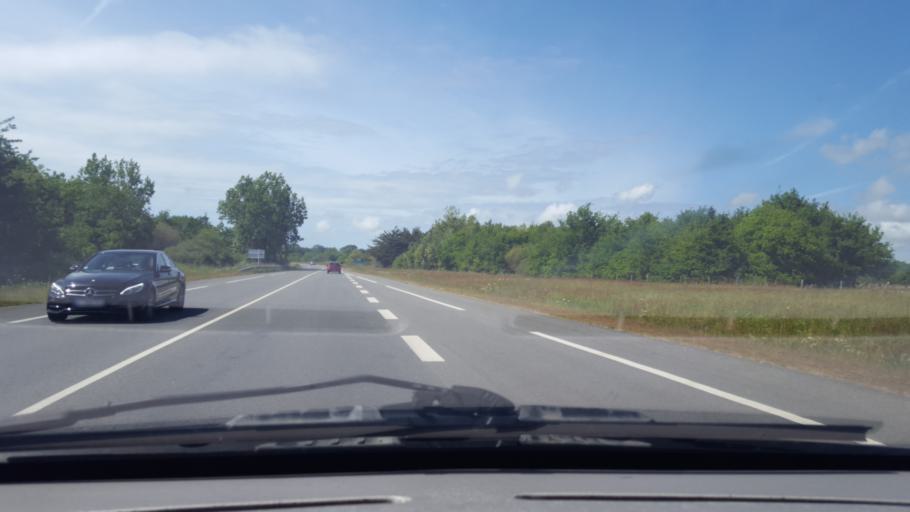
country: FR
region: Pays de la Loire
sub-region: Departement de la Loire-Atlantique
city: Les Moutiers-en-Retz
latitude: 47.0679
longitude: -1.9875
